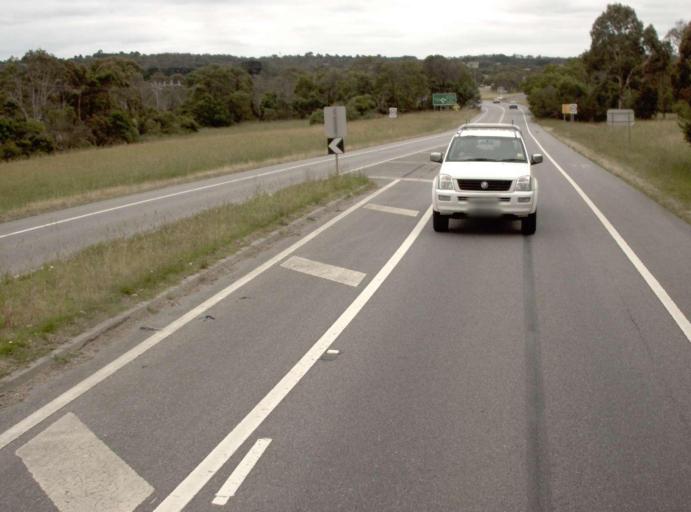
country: AU
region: Victoria
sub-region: Mornington Peninsula
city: Safety Beach
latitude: -38.3066
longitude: 145.0308
